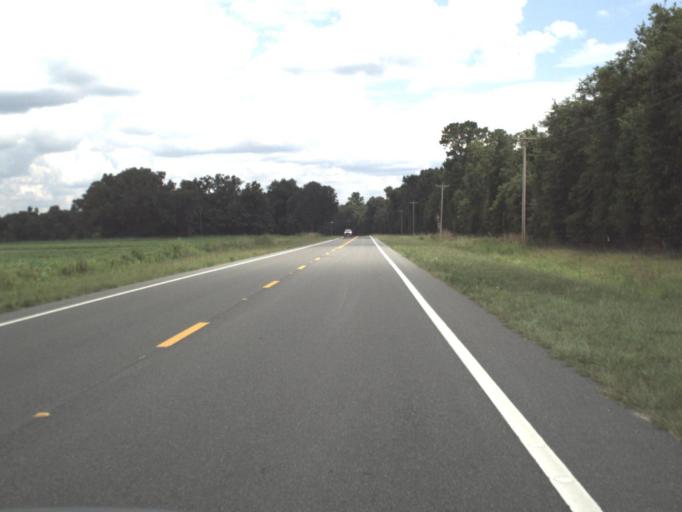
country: US
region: Florida
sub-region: Alachua County
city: Alachua
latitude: 29.8425
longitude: -82.3874
